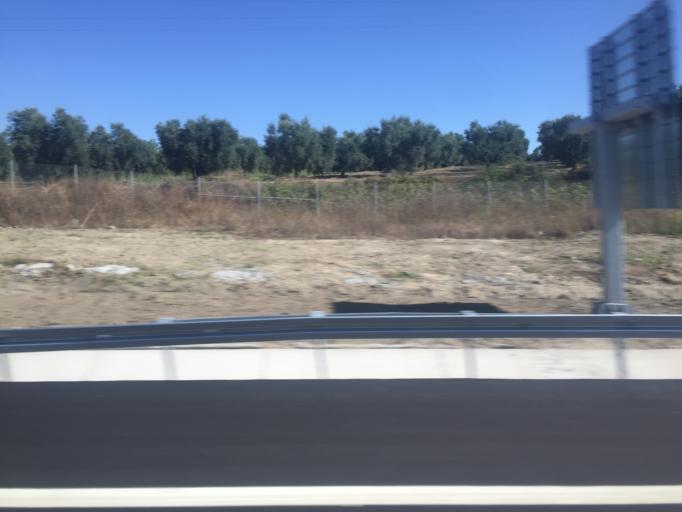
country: TR
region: Bursa
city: Gorukle
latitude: 40.2551
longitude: 28.7381
